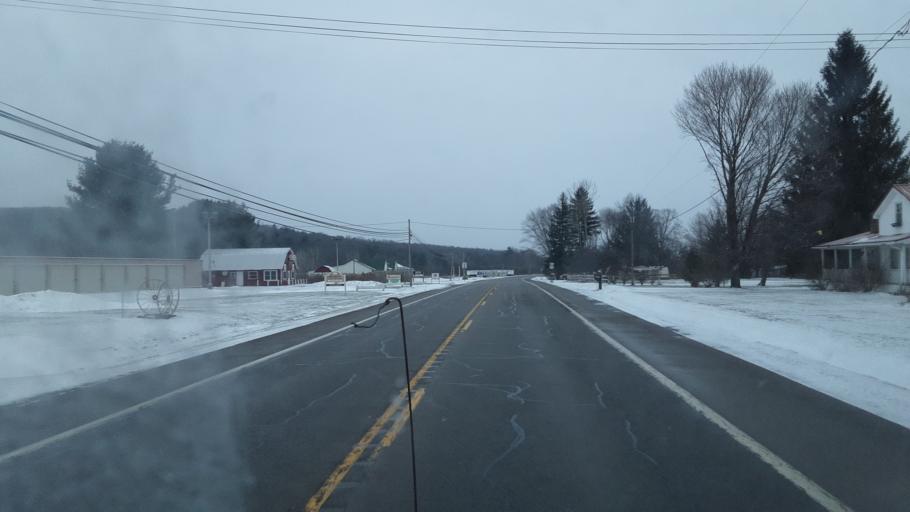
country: US
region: New York
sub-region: Allegany County
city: Belmont
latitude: 42.2335
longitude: -78.0513
